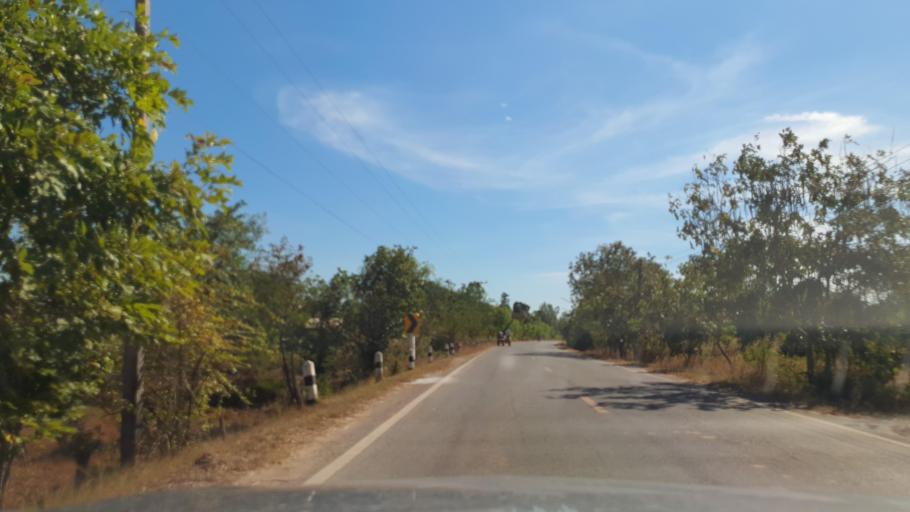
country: TH
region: Kalasin
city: Khao Wong
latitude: 16.7118
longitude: 104.1147
